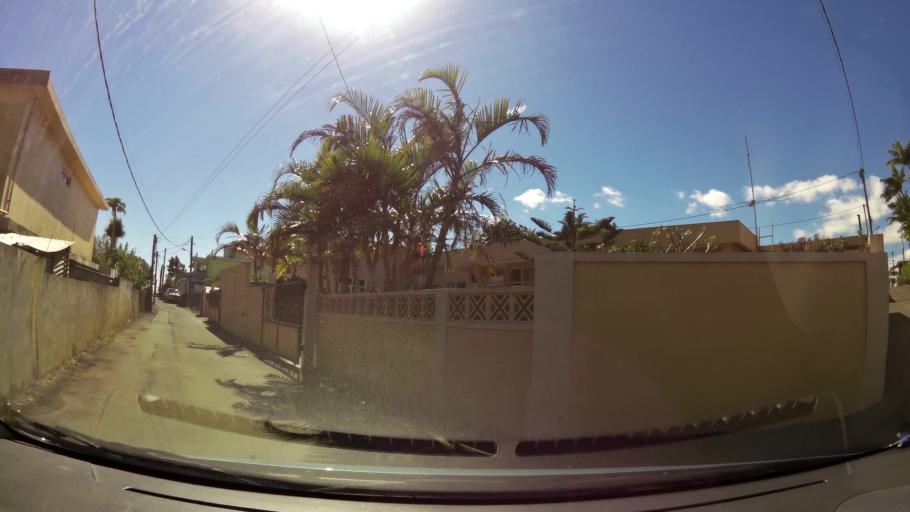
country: MU
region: Plaines Wilhems
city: Curepipe
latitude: -20.3357
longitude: 57.4910
